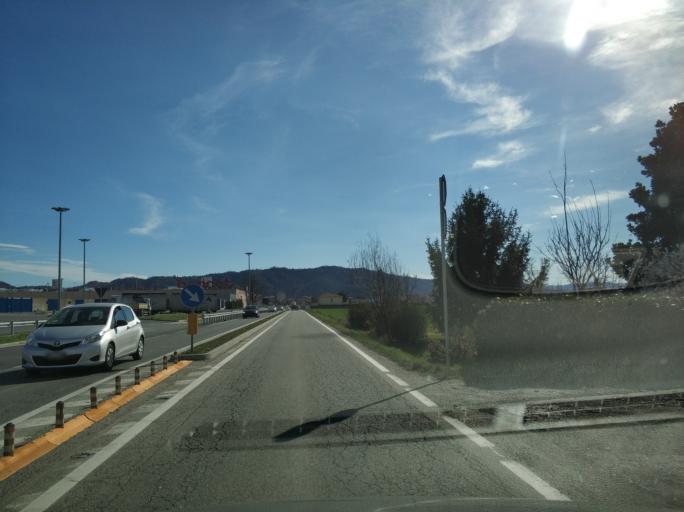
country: IT
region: Piedmont
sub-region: Provincia di Torino
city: Chivasso
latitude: 45.2052
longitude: 7.8899
